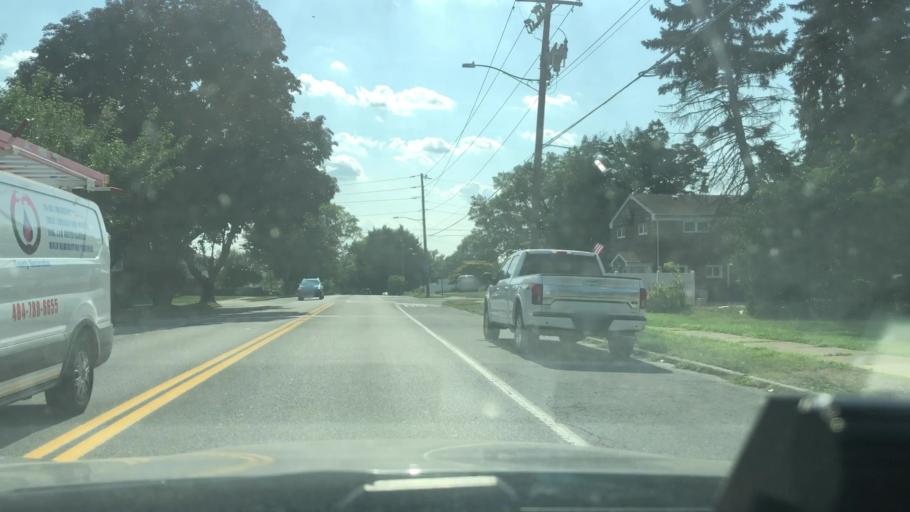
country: US
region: Pennsylvania
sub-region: Northampton County
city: Bethlehem
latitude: 40.6333
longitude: -75.4013
